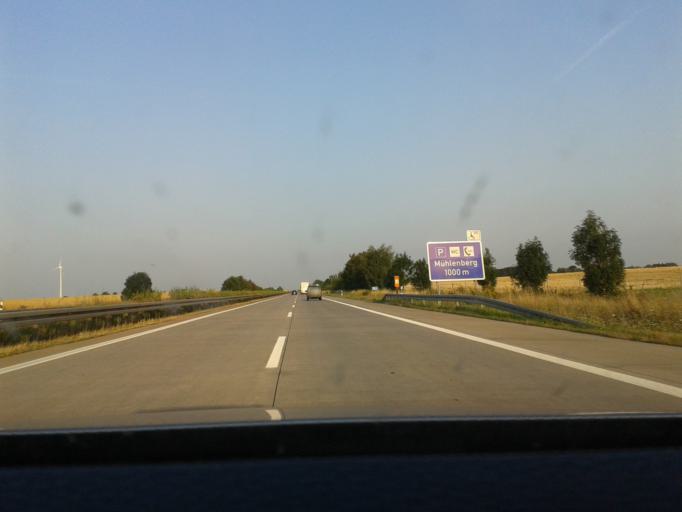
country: DE
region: Saxony
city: Bockelwitz
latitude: 51.1928
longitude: 12.9904
